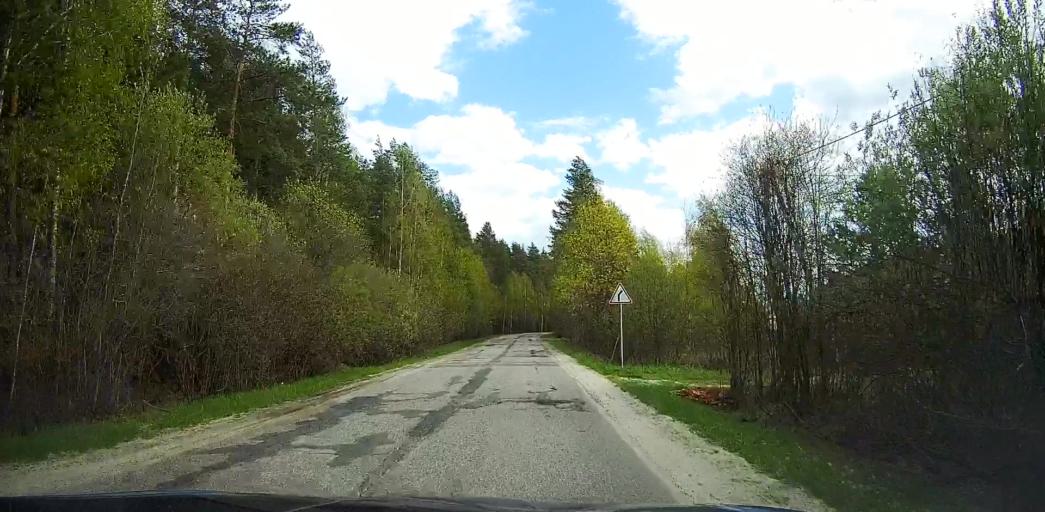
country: RU
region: Moskovskaya
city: Davydovo
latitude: 55.6448
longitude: 38.7719
